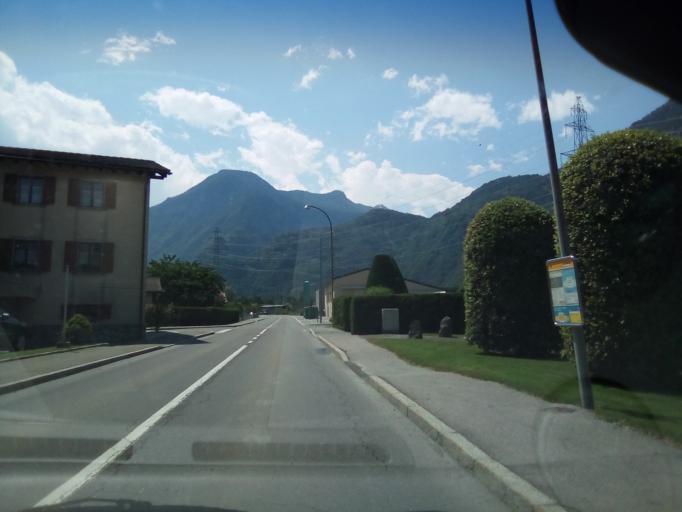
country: CH
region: Valais
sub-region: Saint-Maurice District
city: Vernayaz
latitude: 46.1486
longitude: 7.0421
